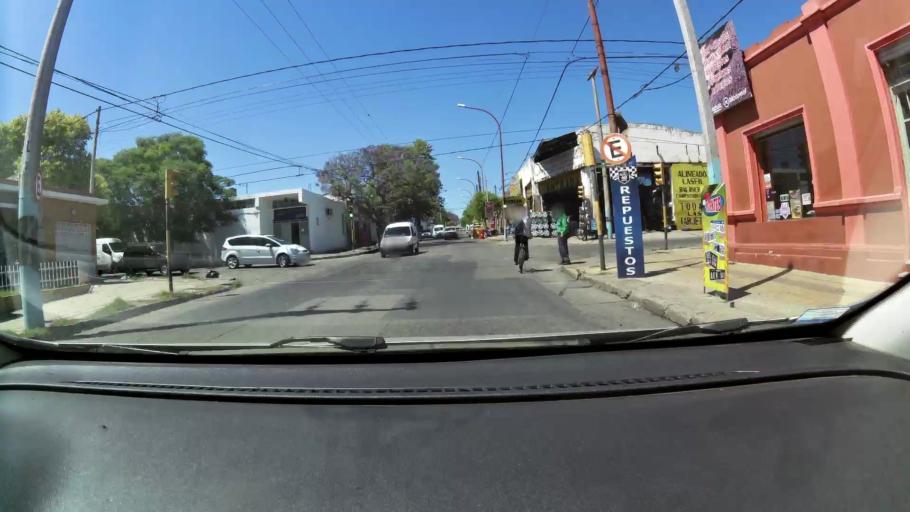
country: AR
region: Cordoba
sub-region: Departamento de Capital
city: Cordoba
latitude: -31.4262
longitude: -64.1510
